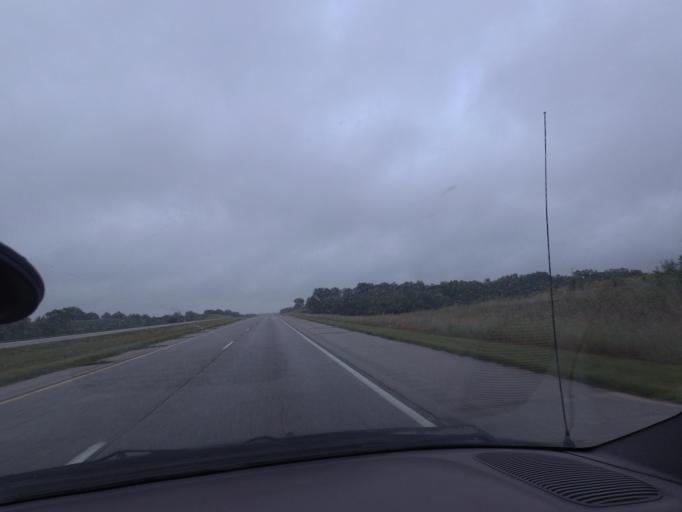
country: US
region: Illinois
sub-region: Pike County
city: Barry
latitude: 39.6928
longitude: -90.9666
